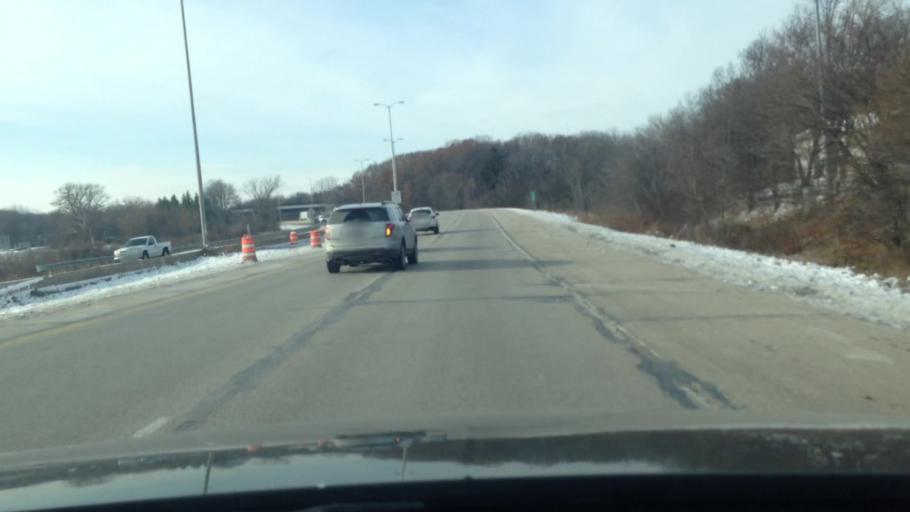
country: US
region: Wisconsin
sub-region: Milwaukee County
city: Hales Corners
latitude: 42.9570
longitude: -88.0522
